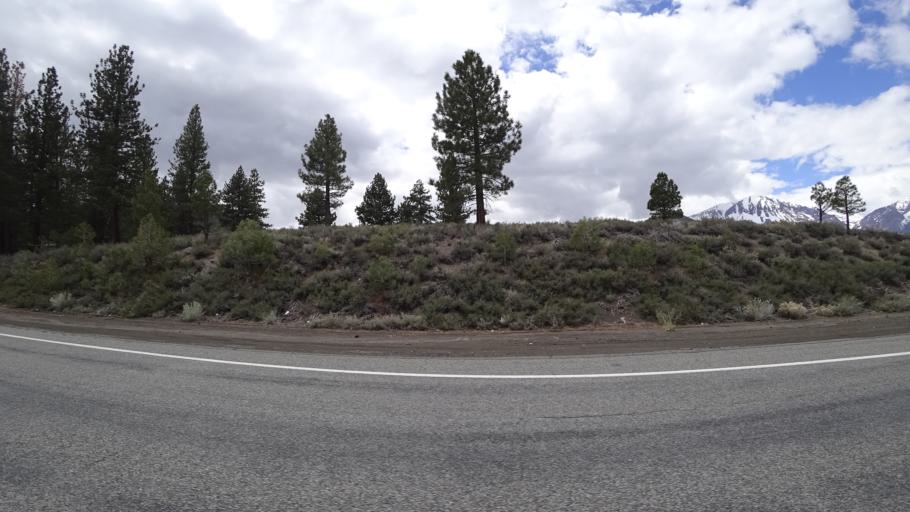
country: US
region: California
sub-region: Mono County
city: Mammoth Lakes
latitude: 37.8137
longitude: -119.0549
